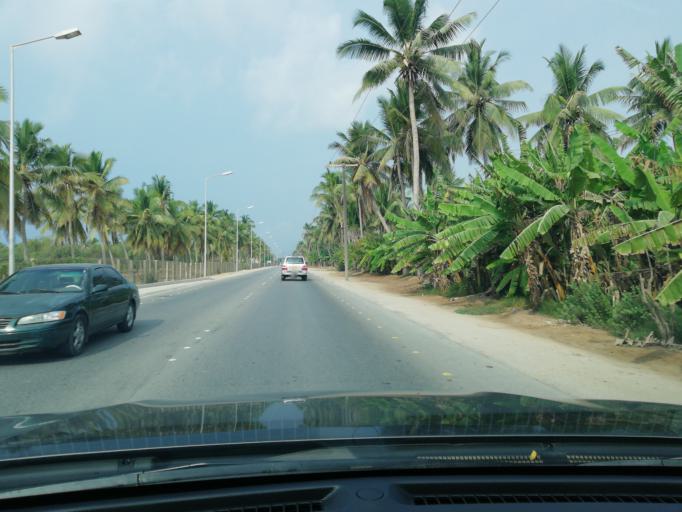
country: OM
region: Zufar
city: Salalah
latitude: 17.0112
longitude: 54.1400
